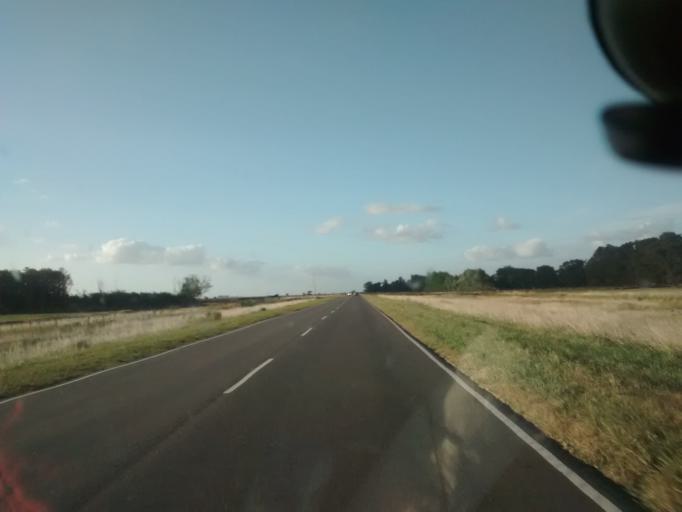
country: AR
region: Buenos Aires
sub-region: Partido de General Belgrano
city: General Belgrano
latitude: -36.0369
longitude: -58.6244
